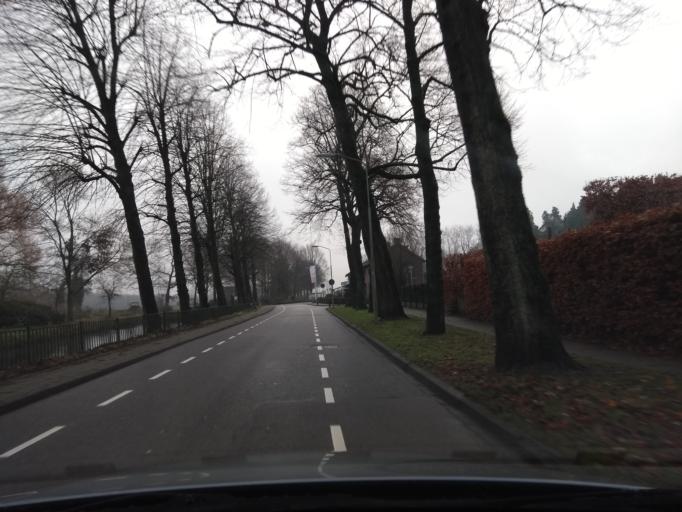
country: NL
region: Gelderland
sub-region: Gemeente Bronckhorst
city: Hengelo
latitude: 52.0510
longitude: 6.3135
